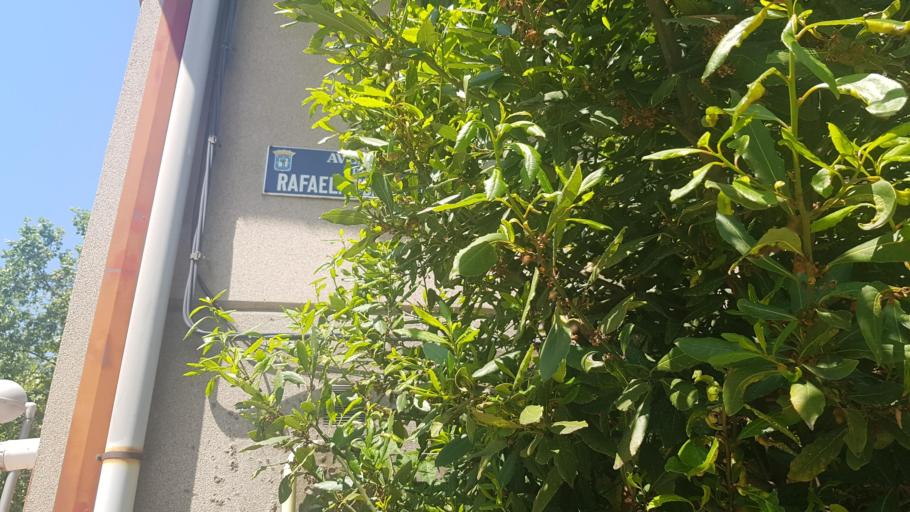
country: ES
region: Madrid
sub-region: Provincia de Madrid
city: Villaverde
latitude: 40.3683
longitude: -3.7125
